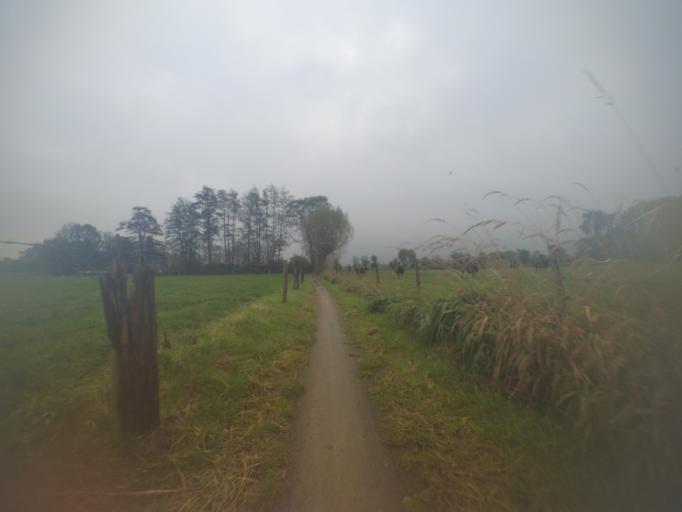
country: NL
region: Gelderland
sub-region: Gemeente Ede
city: Lunteren
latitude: 52.0953
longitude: 5.6003
